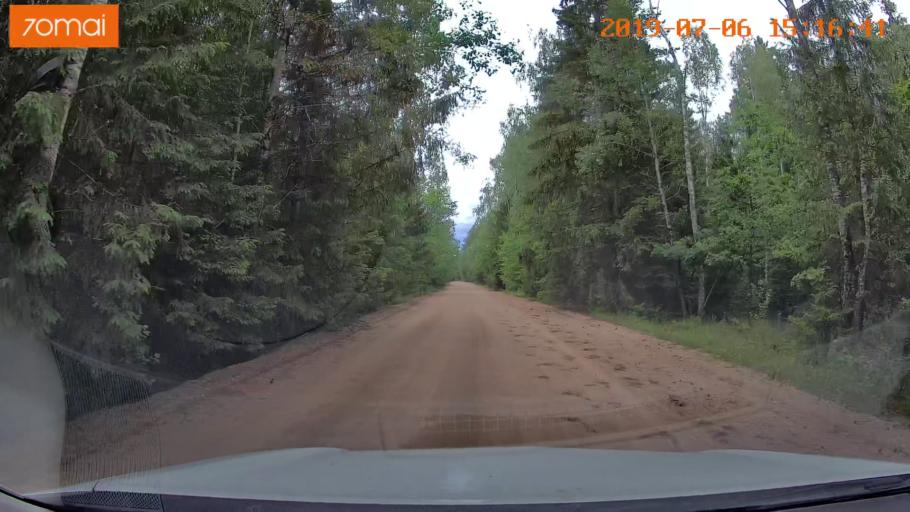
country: BY
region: Minsk
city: Ivyanyets
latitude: 53.9828
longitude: 26.6757
